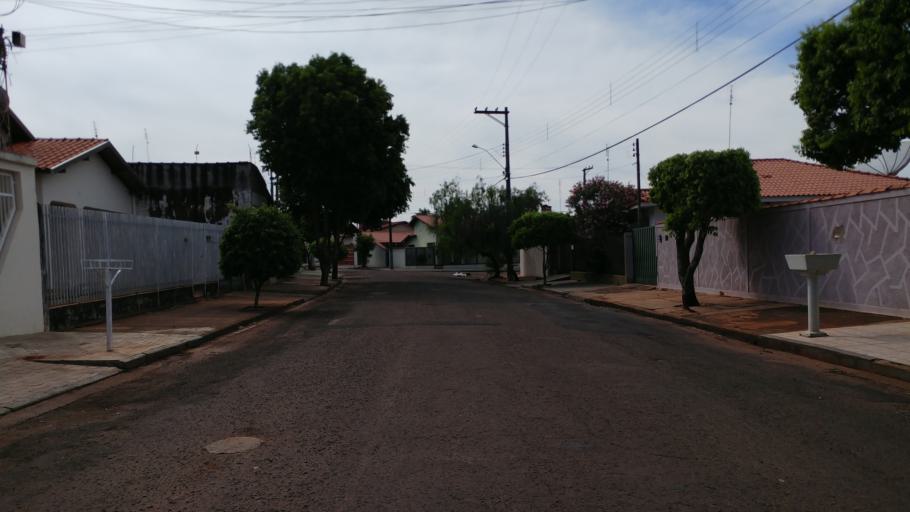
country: BR
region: Sao Paulo
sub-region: Paraguacu Paulista
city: Paraguacu Paulista
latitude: -22.4067
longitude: -50.5777
